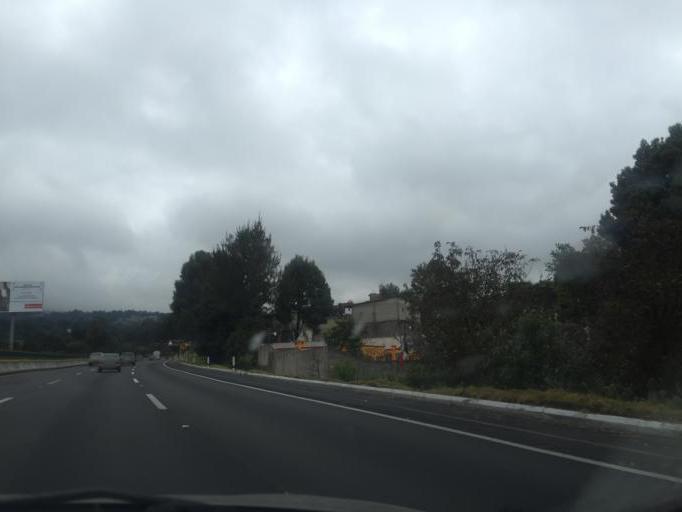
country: MX
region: Mexico City
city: Xochimilco
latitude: 19.1954
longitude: -99.1536
